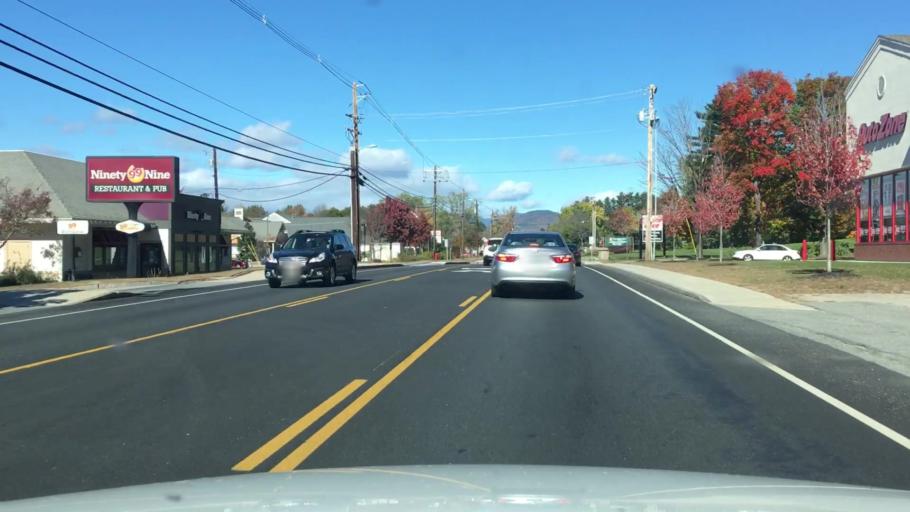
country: US
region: New Hampshire
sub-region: Carroll County
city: North Conway
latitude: 44.0314
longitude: -71.1204
